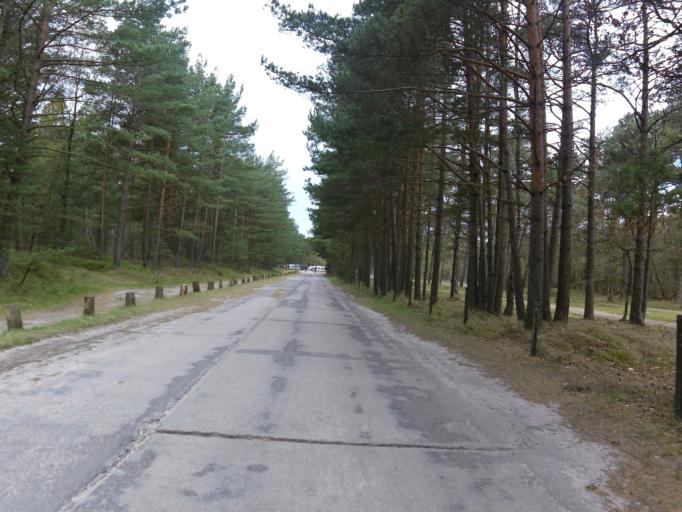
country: DE
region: Mecklenburg-Vorpommern
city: Ostseebad Prerow
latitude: 54.4564
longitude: 12.5406
